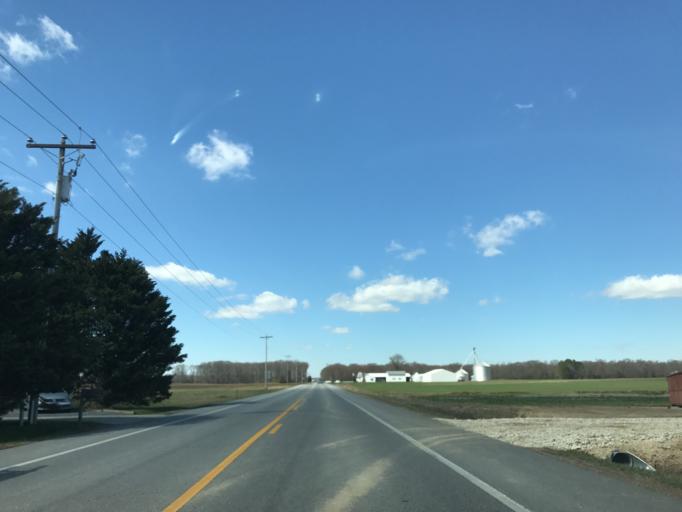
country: US
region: Maryland
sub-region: Caroline County
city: Greensboro
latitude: 39.0937
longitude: -75.8794
